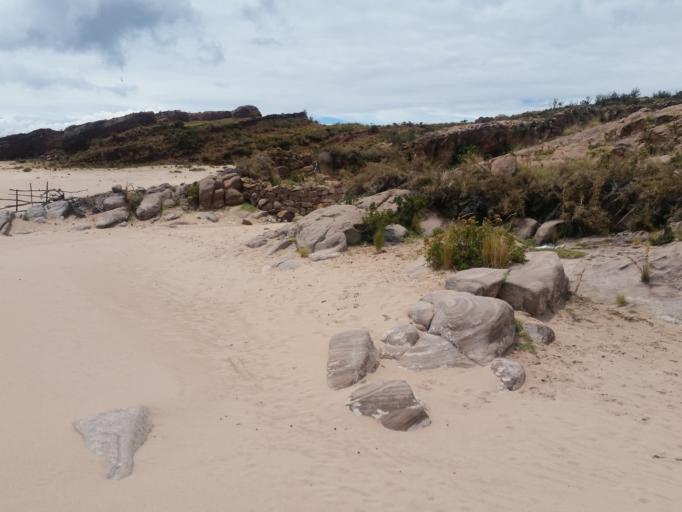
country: PE
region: Puno
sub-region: Provincia de Puno
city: Taquile
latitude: -15.7950
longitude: -69.6806
